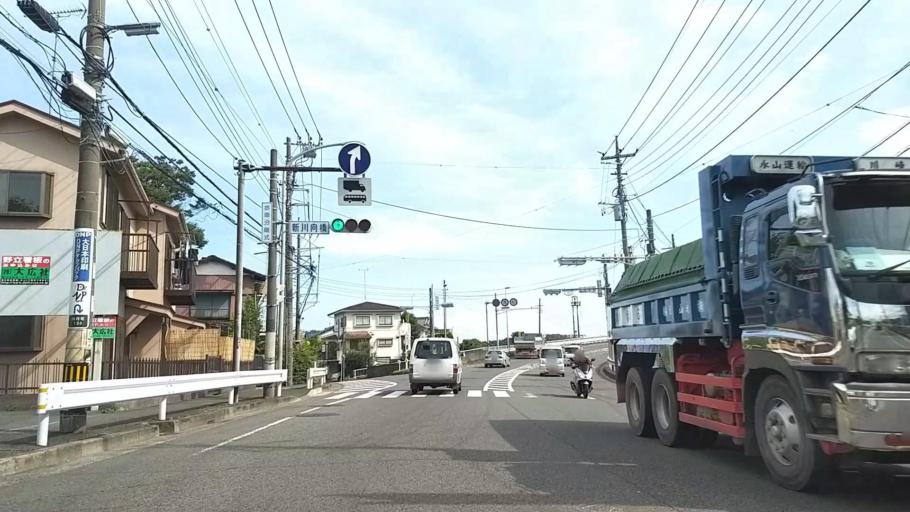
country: JP
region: Kanagawa
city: Yokohama
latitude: 35.5147
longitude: 139.5833
